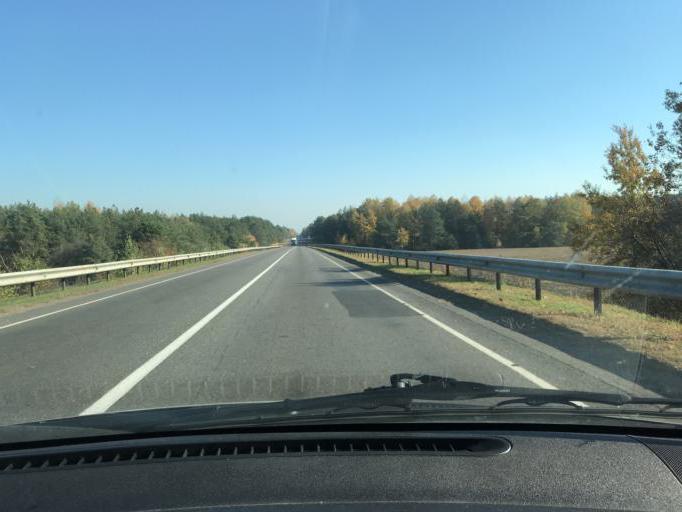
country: BY
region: Brest
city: Davyd-Haradok
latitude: 52.2363
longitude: 27.2553
